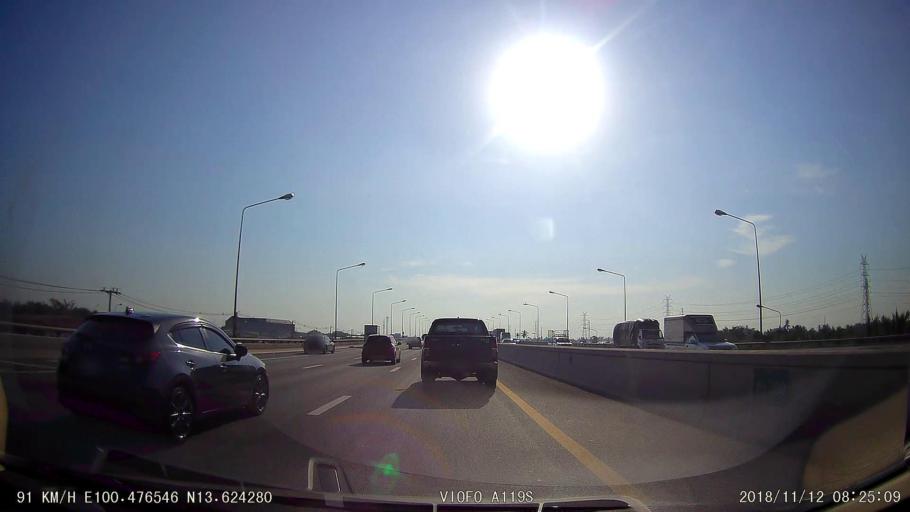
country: TH
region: Bangkok
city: Thung Khru
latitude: 13.6242
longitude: 100.4768
